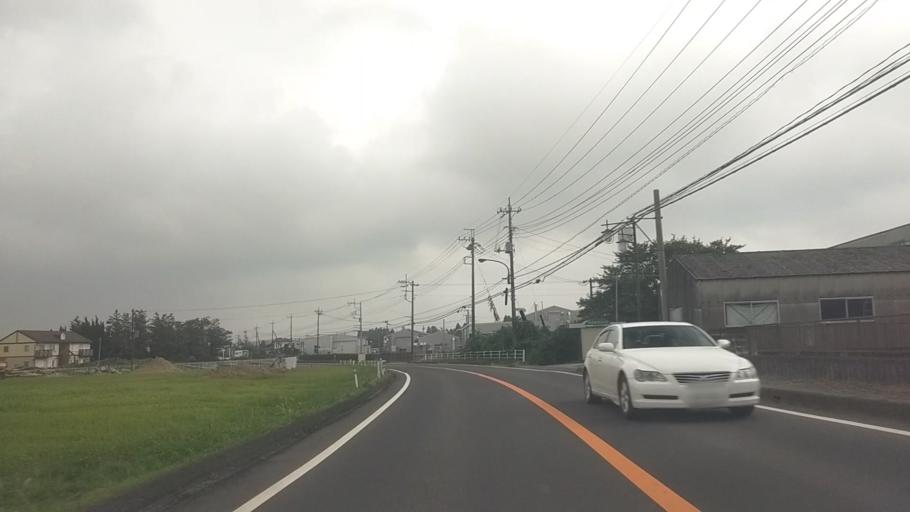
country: JP
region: Chiba
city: Ohara
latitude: 35.2811
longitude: 140.2976
